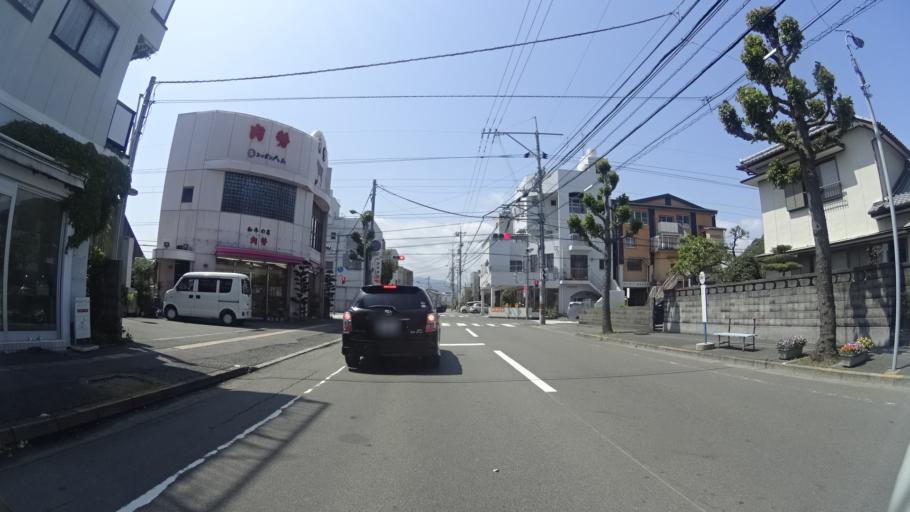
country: JP
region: Tokushima
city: Tokushima-shi
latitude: 34.0603
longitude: 134.5514
